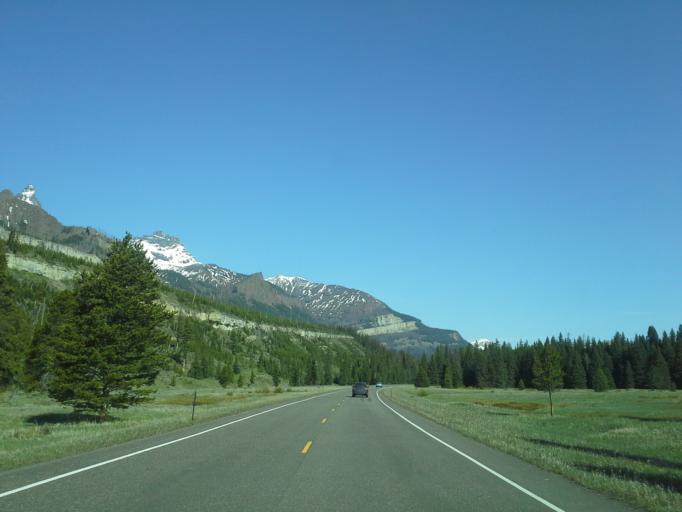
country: US
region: Montana
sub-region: Carbon County
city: Red Lodge
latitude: 44.9621
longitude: -109.8202
